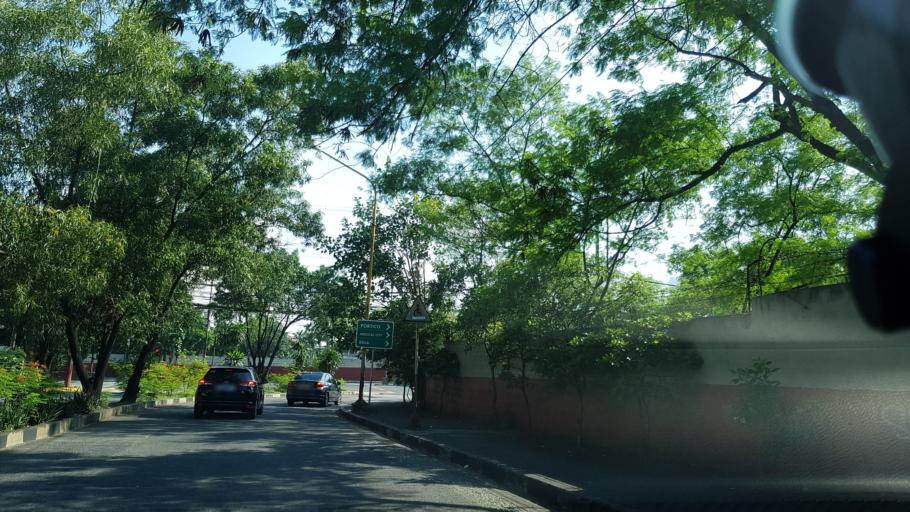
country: PH
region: Metro Manila
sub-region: Pasig
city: Pasig City
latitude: 14.5899
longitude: 121.0725
